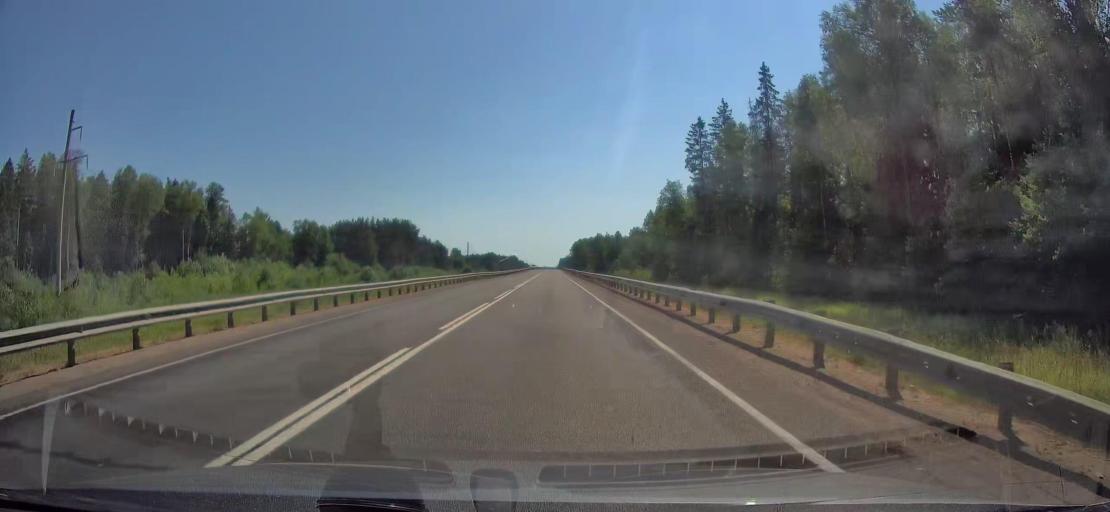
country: RU
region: Vologda
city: Chagoda
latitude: 59.0153
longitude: 35.4173
